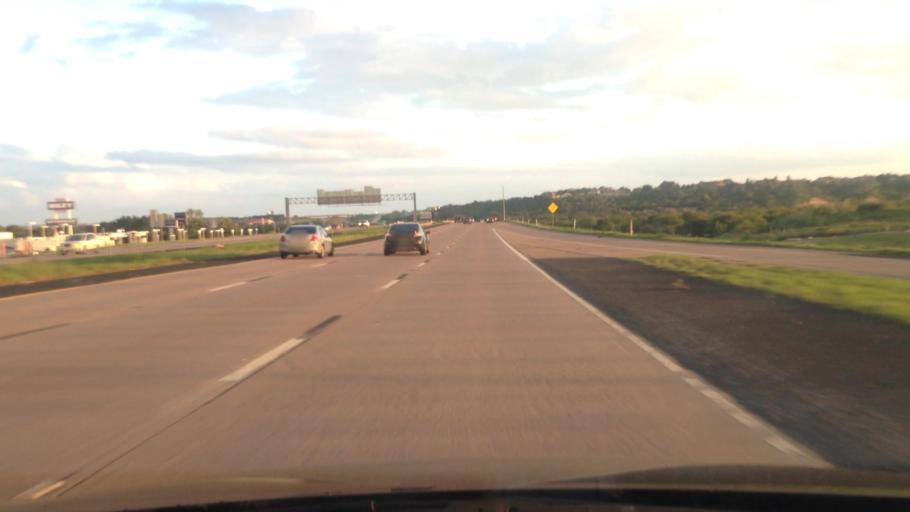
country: US
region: Texas
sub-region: Tarrant County
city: White Settlement
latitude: 32.7221
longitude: -97.4801
